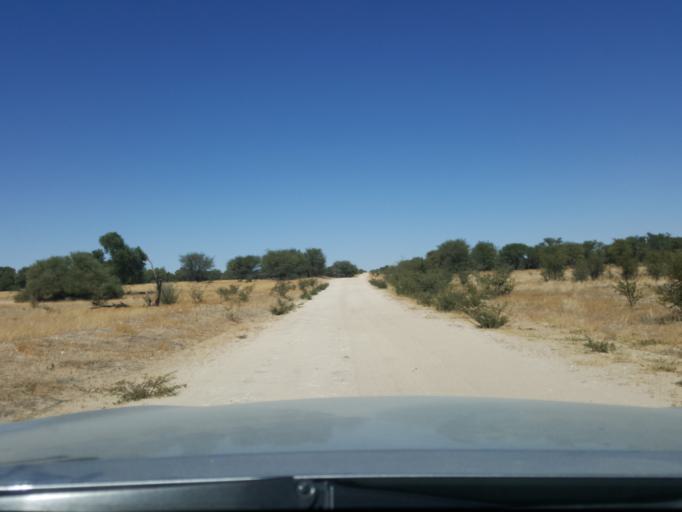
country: BW
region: Kgalagadi
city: Hukuntsi
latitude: -23.9822
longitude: 21.2085
